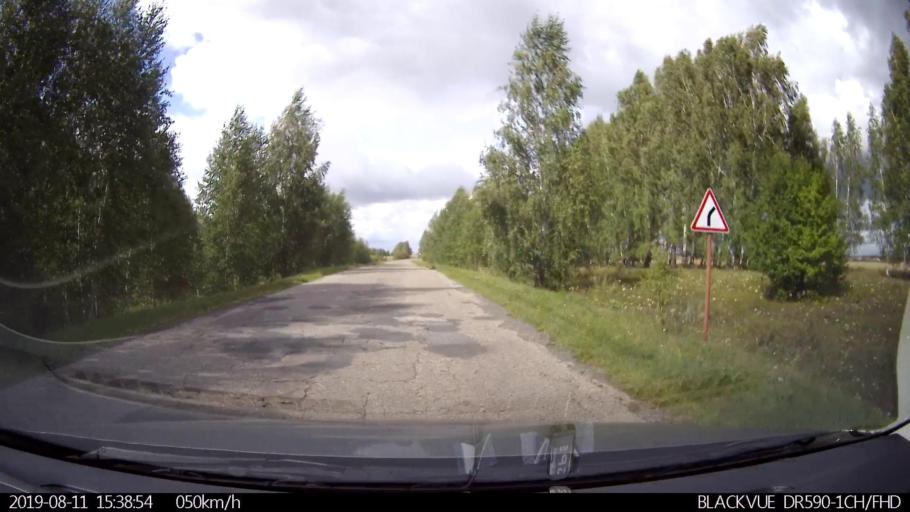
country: RU
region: Ulyanovsk
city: Ignatovka
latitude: 53.8647
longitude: 47.6398
